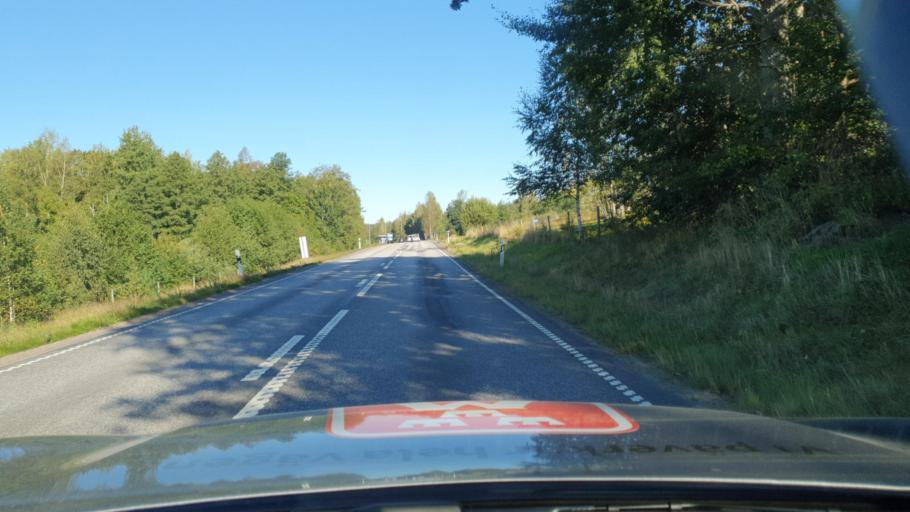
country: SE
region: OEstergoetland
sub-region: Linkopings Kommun
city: Ljungsbro
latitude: 58.7784
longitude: 15.5099
